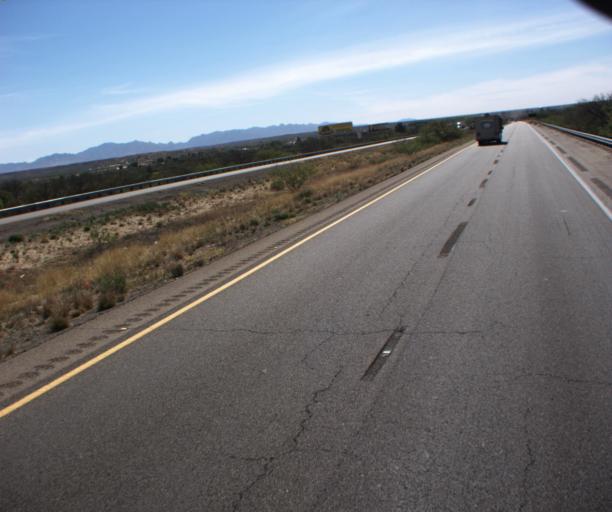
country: US
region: Arizona
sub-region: Cochise County
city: Benson
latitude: 31.9736
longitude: -110.2869
